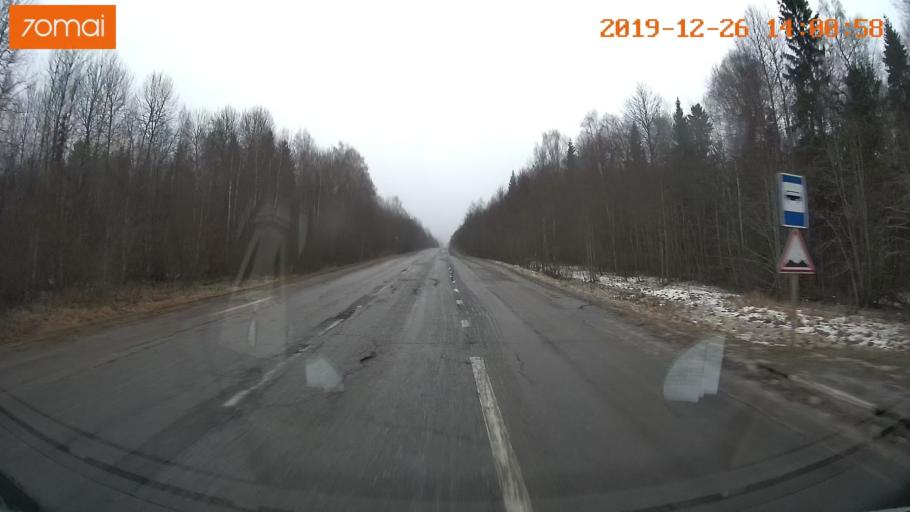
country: RU
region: Jaroslavl
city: Poshekhon'ye
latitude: 58.5541
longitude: 38.7541
